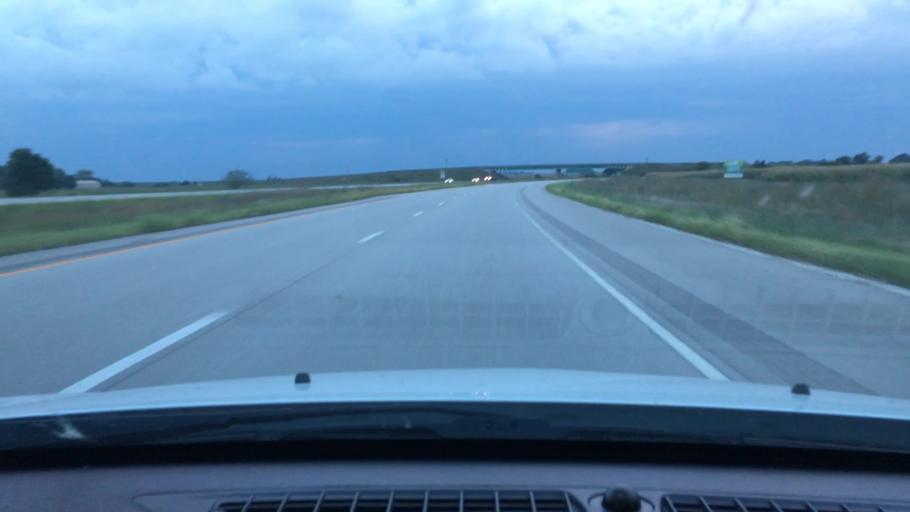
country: US
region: Illinois
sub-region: Sangamon County
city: New Berlin
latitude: 39.7378
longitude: -89.9799
